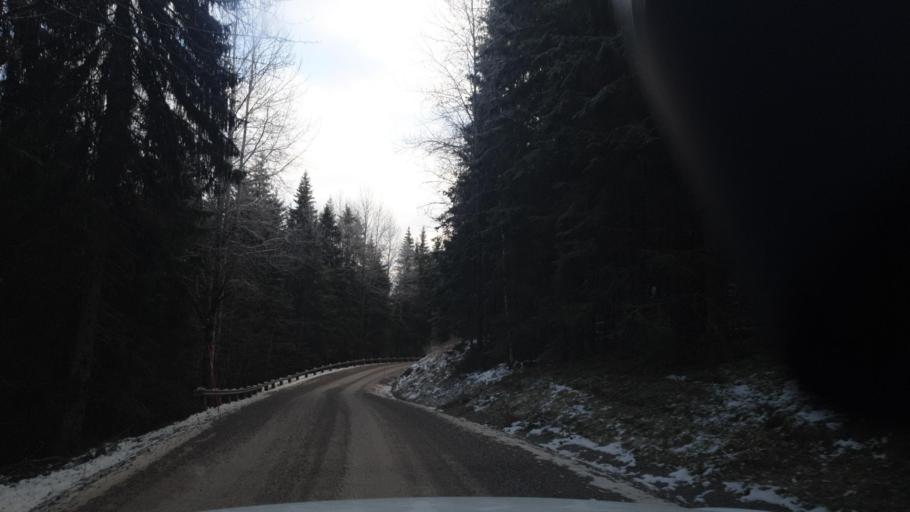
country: SE
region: Vaermland
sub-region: Eda Kommun
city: Charlottenberg
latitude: 60.0632
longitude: 12.5445
